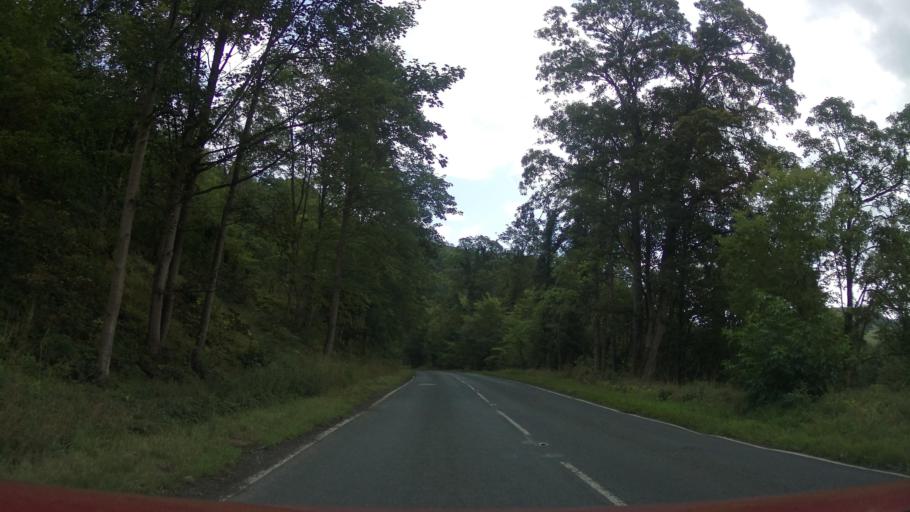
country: GB
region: England
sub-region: North Yorkshire
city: Leyburn
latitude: 54.3908
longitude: -1.8274
